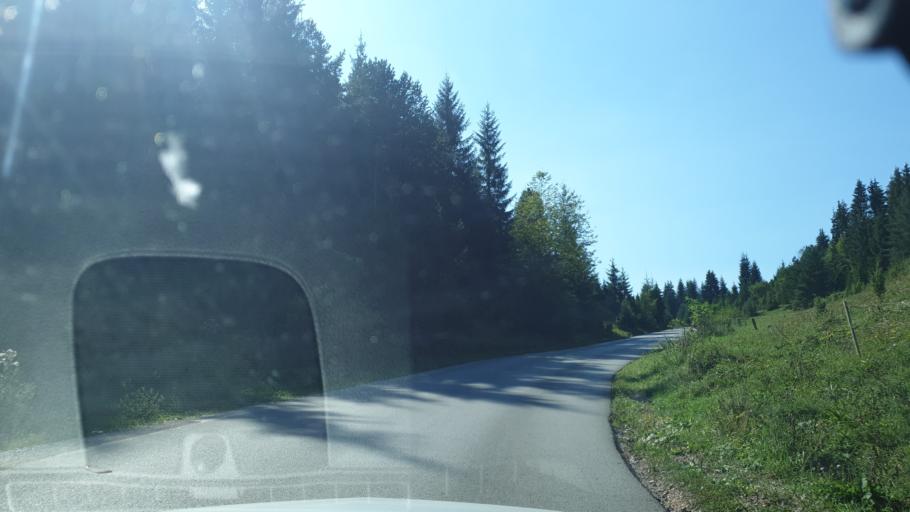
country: RS
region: Central Serbia
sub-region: Zlatiborski Okrug
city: Nova Varos
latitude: 43.4312
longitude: 19.8735
